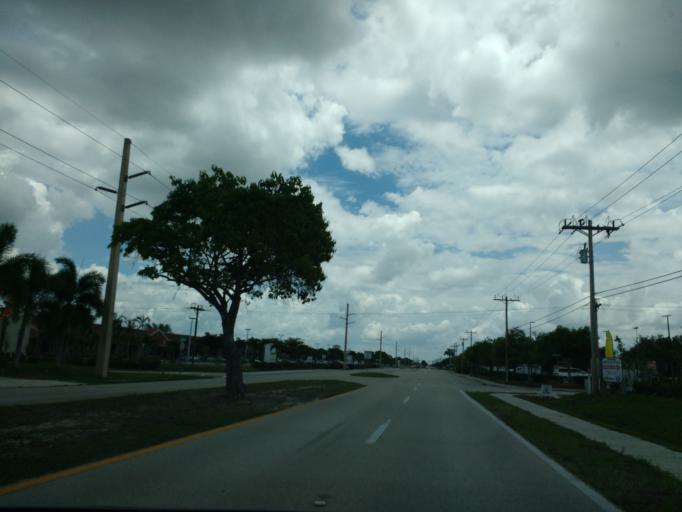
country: US
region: Florida
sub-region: Lee County
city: Cape Coral
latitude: 26.5627
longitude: -82.0115
